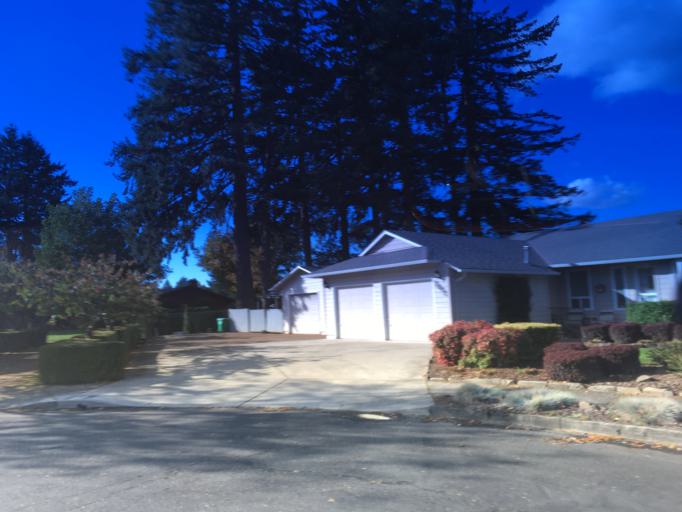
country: US
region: Oregon
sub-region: Multnomah County
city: Gresham
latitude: 45.5011
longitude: -122.3931
